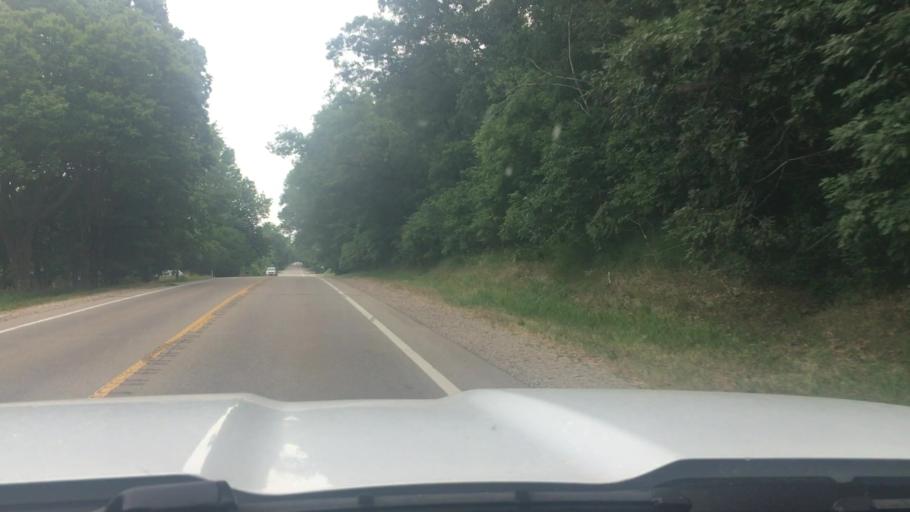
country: US
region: Michigan
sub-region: Ionia County
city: Saranac
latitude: 42.9370
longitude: -85.2208
